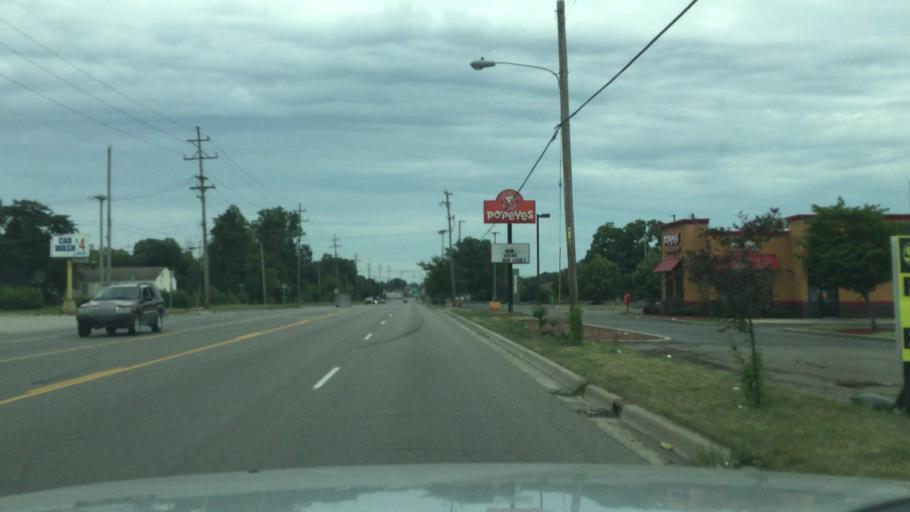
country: US
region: Michigan
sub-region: Genesee County
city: Beecher
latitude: 43.0587
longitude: -83.7334
